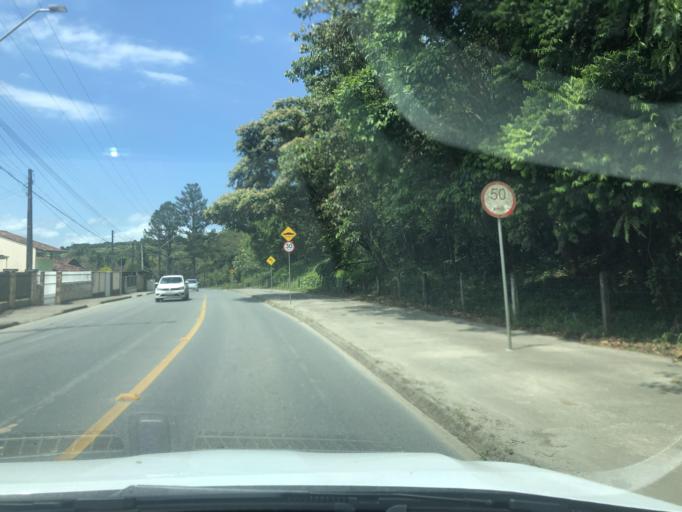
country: BR
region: Santa Catarina
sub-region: Joinville
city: Joinville
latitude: -26.3527
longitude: -48.7875
